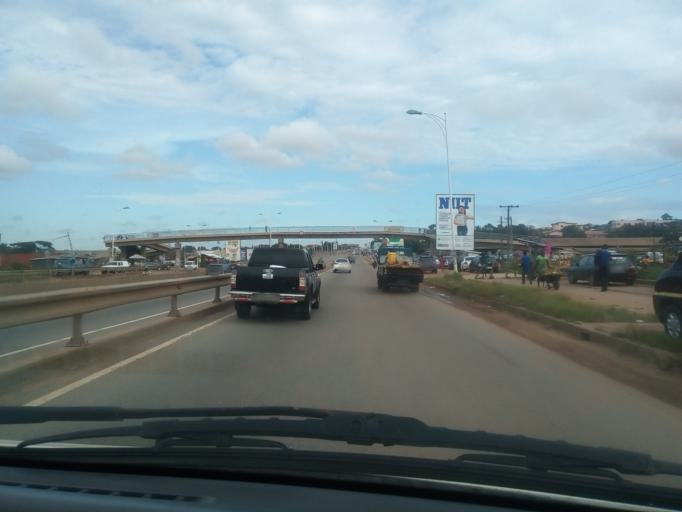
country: GH
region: Greater Accra
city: Dome
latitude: 5.6502
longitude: -0.2542
